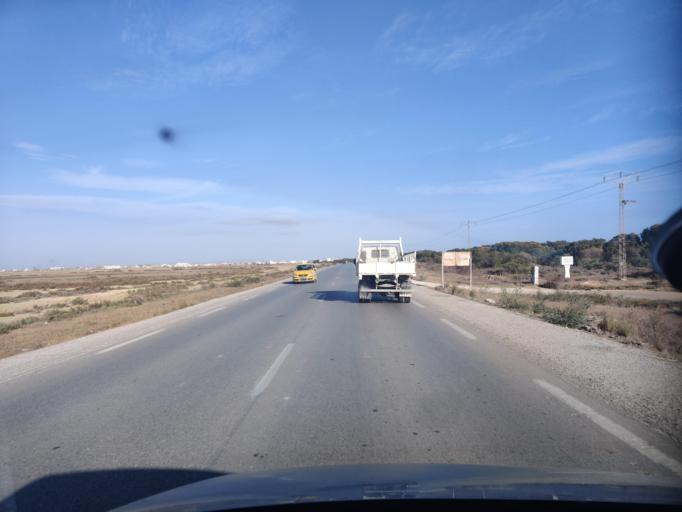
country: TN
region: Ariana
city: Ariana
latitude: 36.9433
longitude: 10.2460
